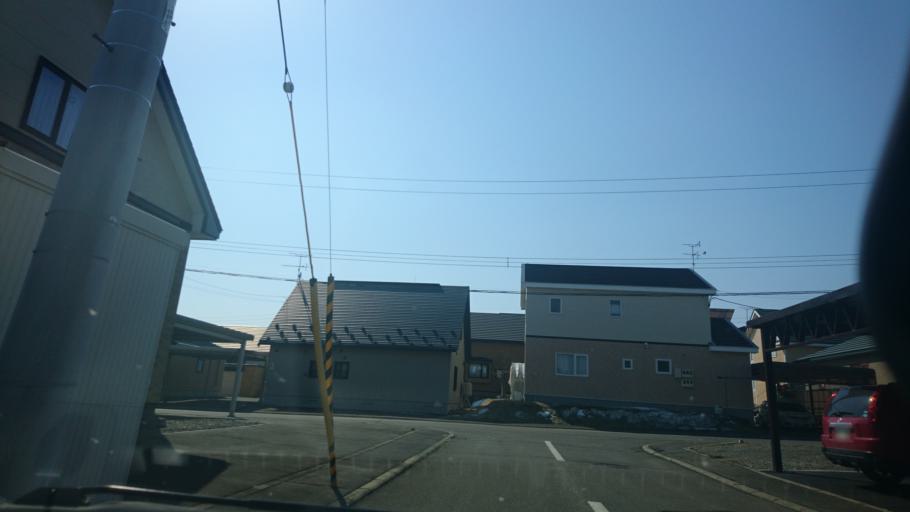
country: JP
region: Hokkaido
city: Obihiro
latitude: 42.9106
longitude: 143.0709
